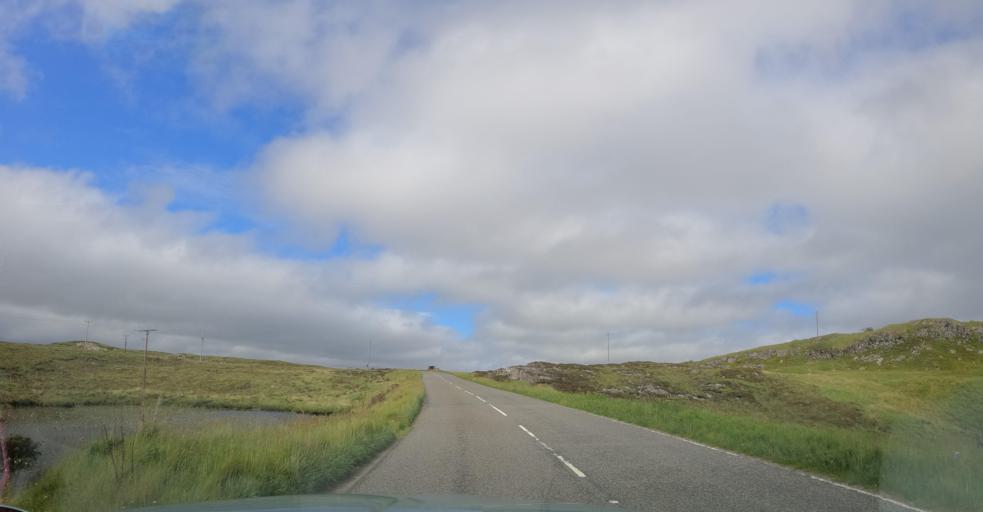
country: GB
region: Scotland
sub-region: Eilean Siar
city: Stornoway
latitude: 58.1099
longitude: -6.5100
